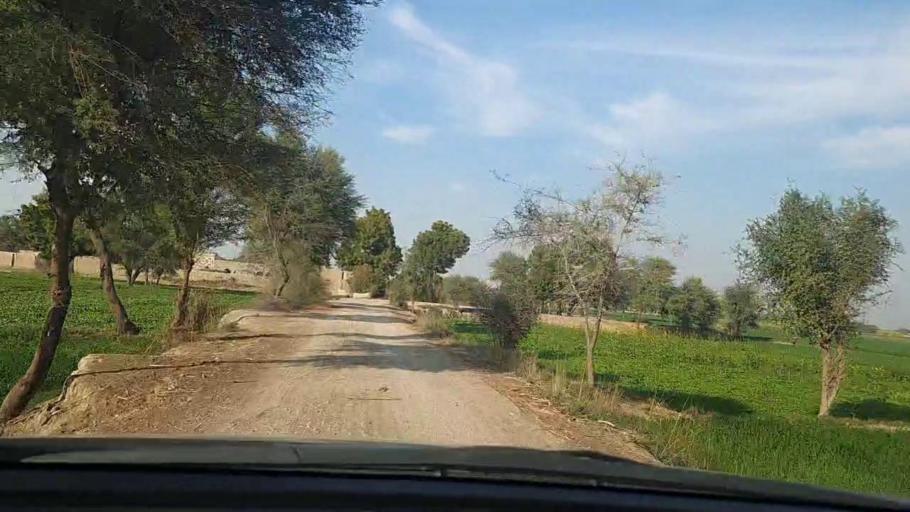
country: PK
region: Sindh
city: Daulatpur
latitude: 26.3168
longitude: 68.0204
